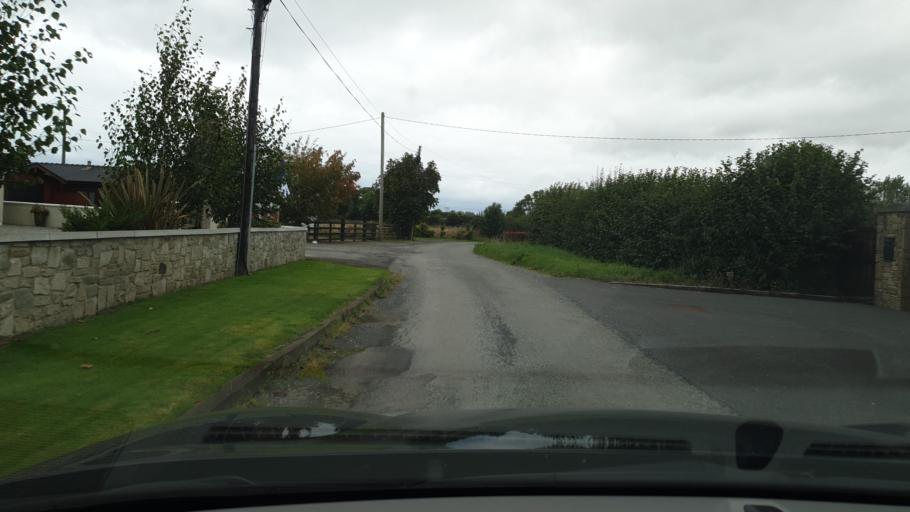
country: IE
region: Leinster
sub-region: Kildare
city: Maynooth
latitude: 53.3383
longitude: -6.6385
